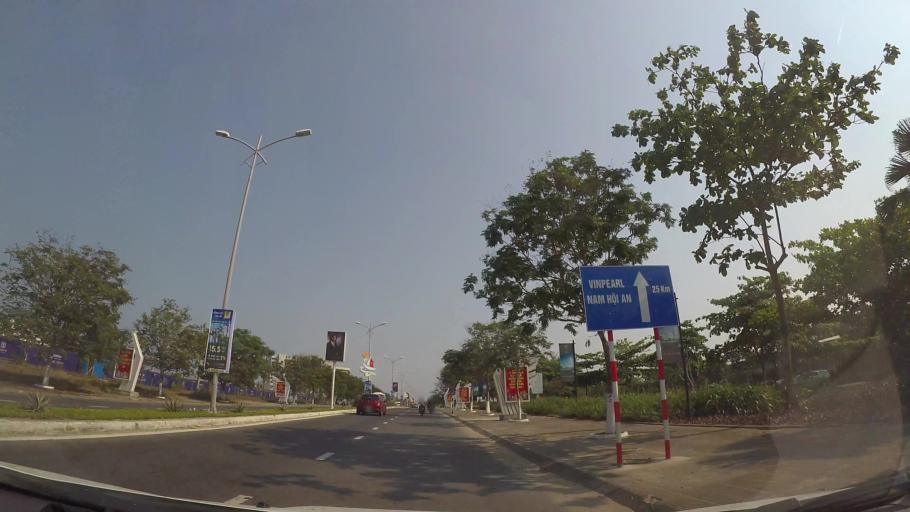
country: VN
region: Da Nang
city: Ngu Hanh Son
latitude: 15.9655
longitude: 108.2858
